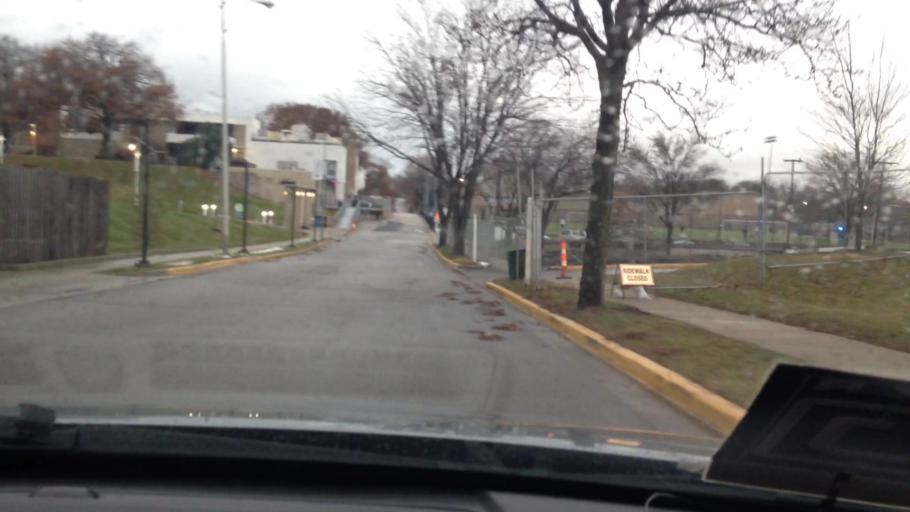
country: US
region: Kansas
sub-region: Johnson County
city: Westwood
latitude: 39.0299
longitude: -94.5713
